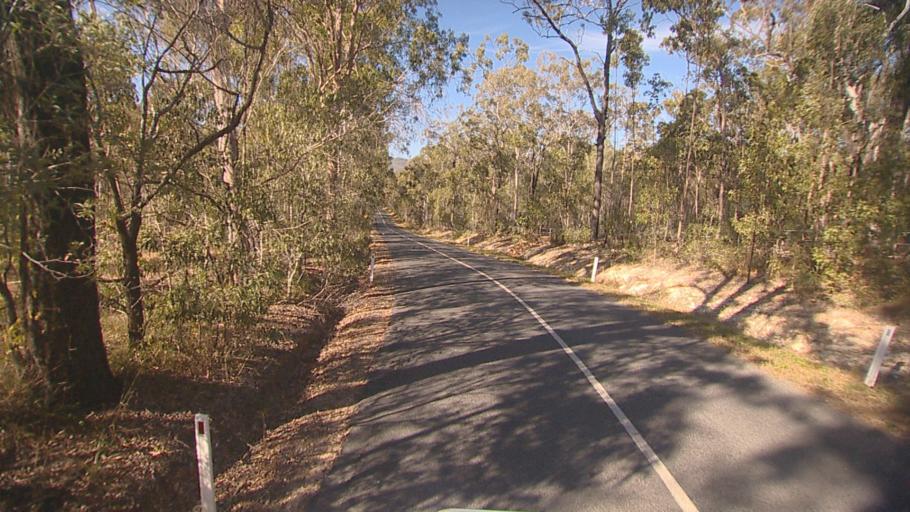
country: AU
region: Queensland
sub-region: Gold Coast
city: Ormeau Hills
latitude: -27.8194
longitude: 153.1691
